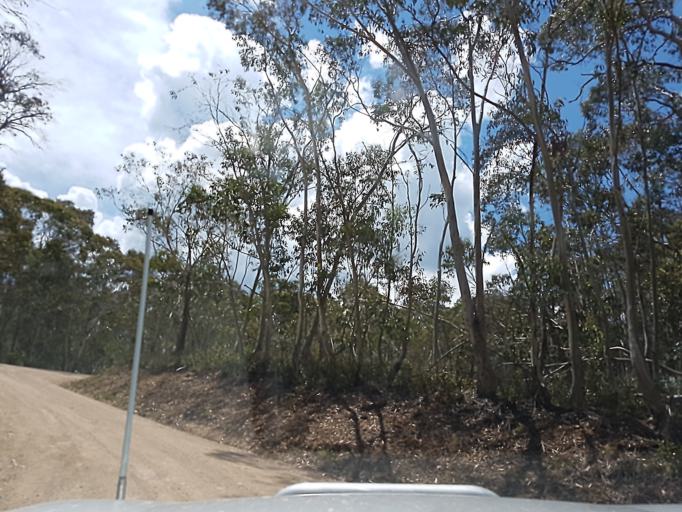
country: AU
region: New South Wales
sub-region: Snowy River
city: Jindabyne
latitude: -36.8977
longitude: 148.0924
